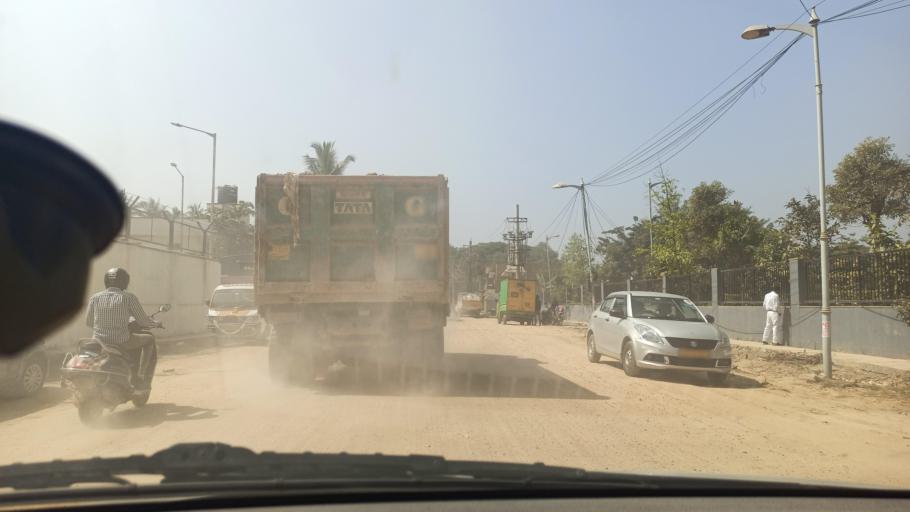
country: IN
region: Karnataka
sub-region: Bangalore Urban
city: Bangalore
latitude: 12.9393
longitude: 77.6891
